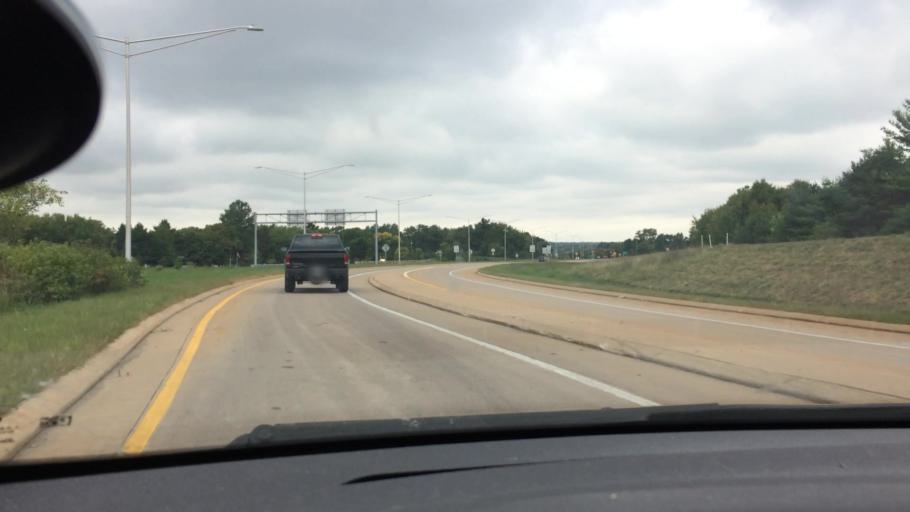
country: US
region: Wisconsin
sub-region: Chippewa County
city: Chippewa Falls
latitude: 44.9215
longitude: -91.3805
